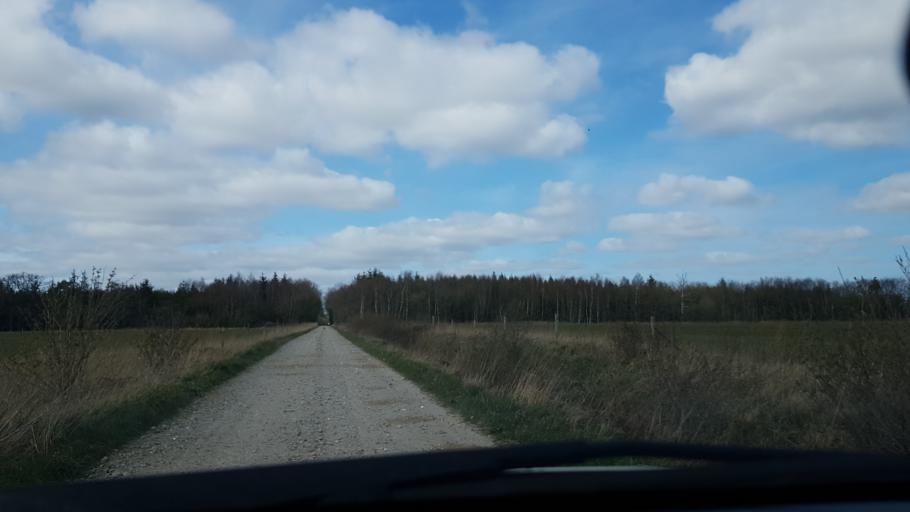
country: DK
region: South Denmark
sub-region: Haderslev Kommune
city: Gram
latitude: 55.2953
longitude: 8.9853
